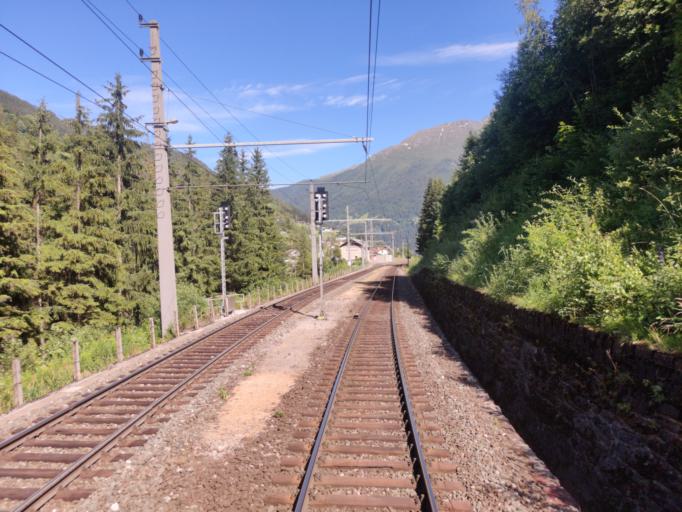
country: AT
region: Tyrol
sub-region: Politischer Bezirk Landeck
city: Strengen
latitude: 47.1267
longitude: 10.4557
